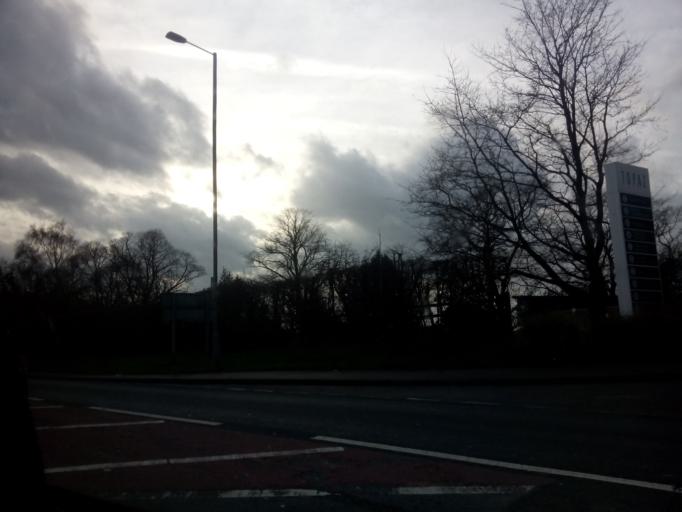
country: GB
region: England
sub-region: Worcestershire
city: Bromsgrove
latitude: 52.3577
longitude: -2.0461
